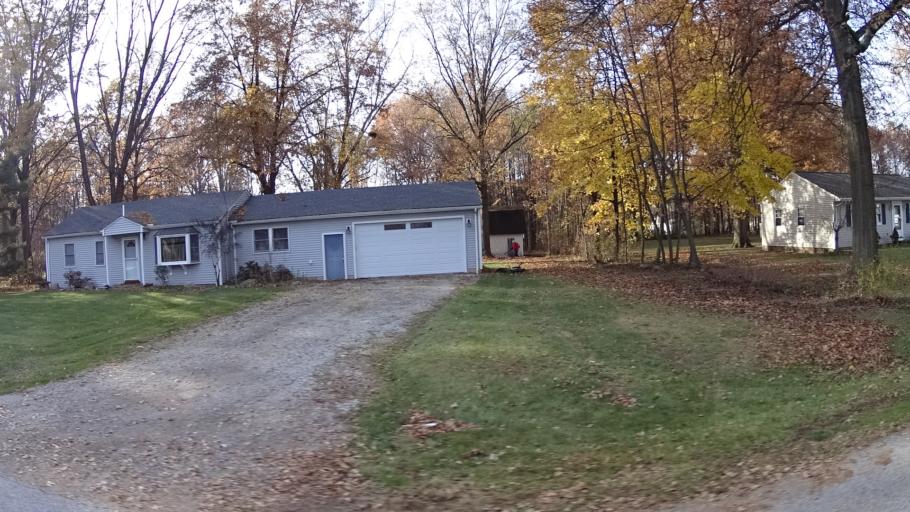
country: US
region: Ohio
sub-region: Lorain County
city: Avon
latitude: 41.4599
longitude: -82.0308
